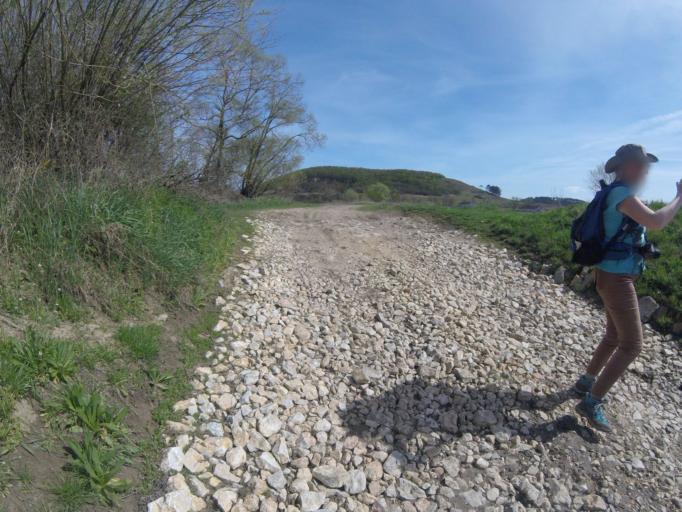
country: HU
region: Borsod-Abauj-Zemplen
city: Szendro
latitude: 48.4223
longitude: 20.7295
